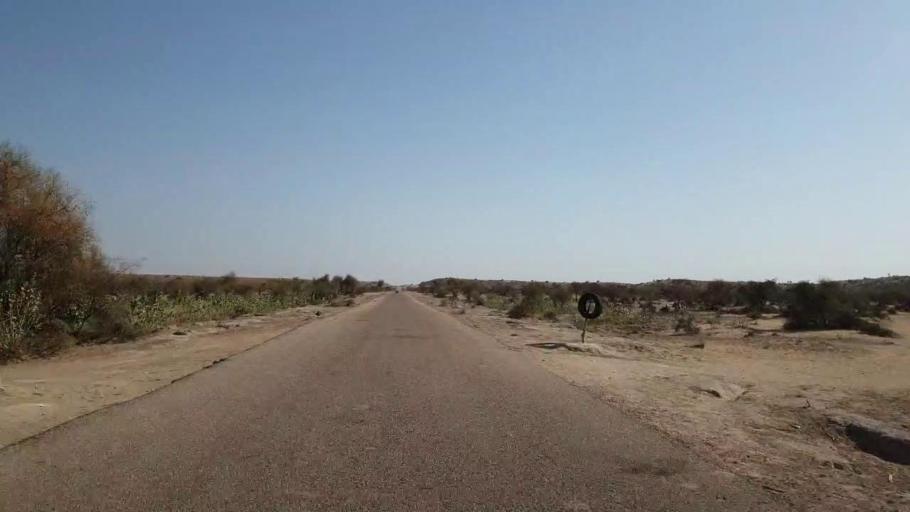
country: PK
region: Sindh
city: Nabisar
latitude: 25.0914
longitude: 70.0400
